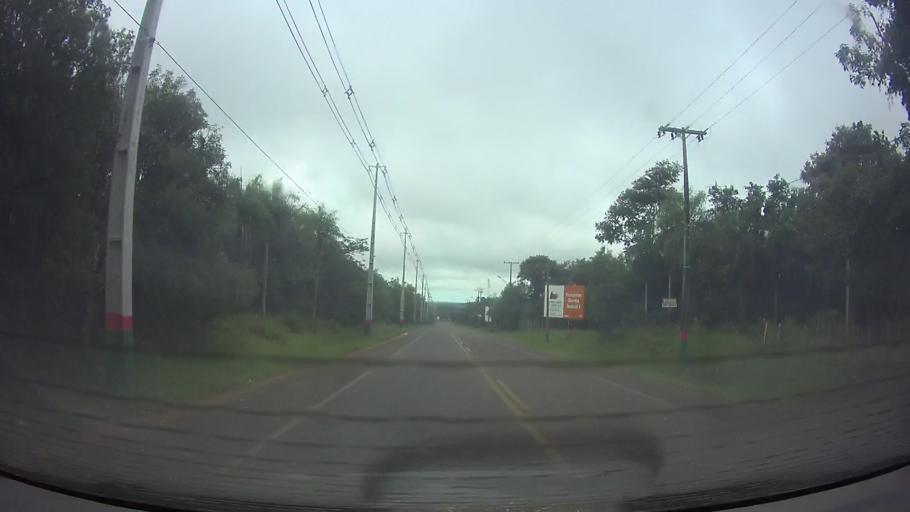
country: PY
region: Cordillera
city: Altos
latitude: -25.2727
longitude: -57.2587
